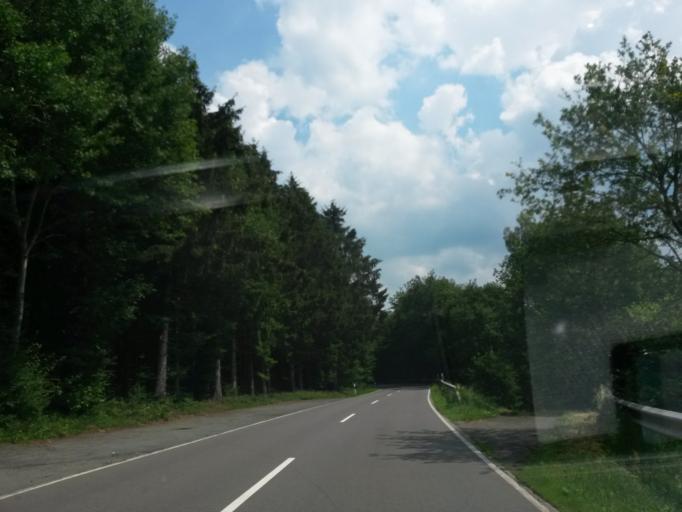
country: DE
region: North Rhine-Westphalia
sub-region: Regierungsbezirk Arnsberg
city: Olpe
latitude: 51.0708
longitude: 7.8856
